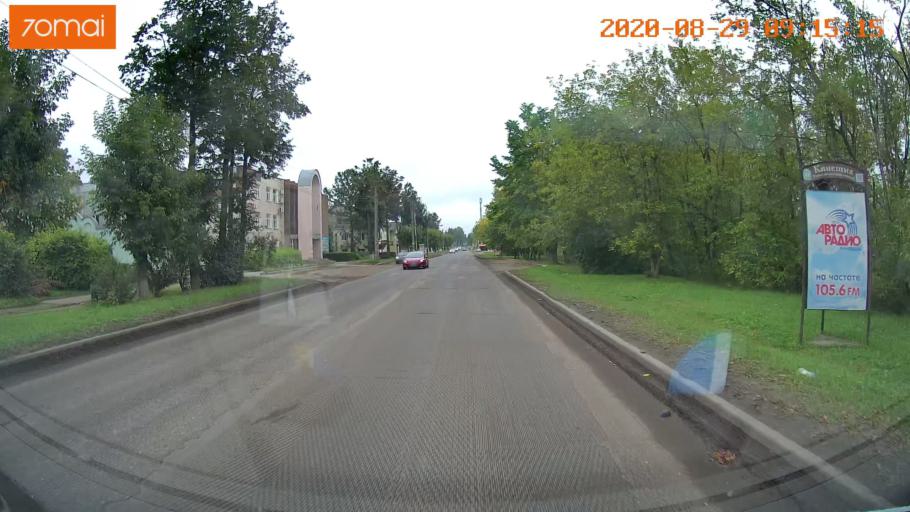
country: RU
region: Ivanovo
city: Kineshma
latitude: 57.4376
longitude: 42.1272
